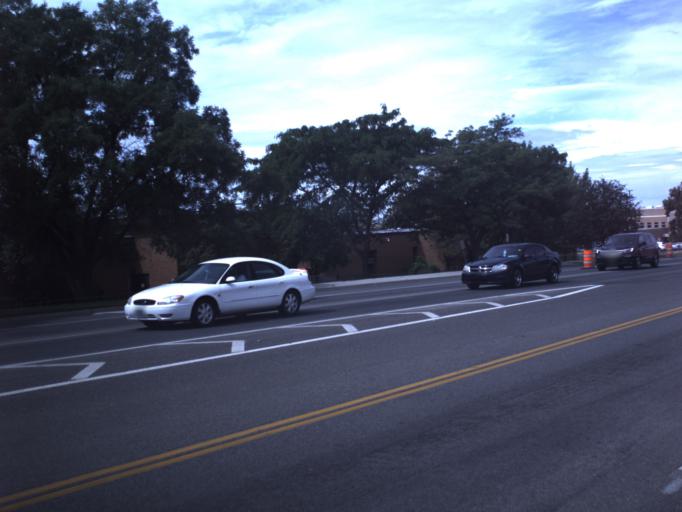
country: US
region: Utah
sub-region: Davis County
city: Clearfield
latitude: 41.1036
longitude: -112.0074
